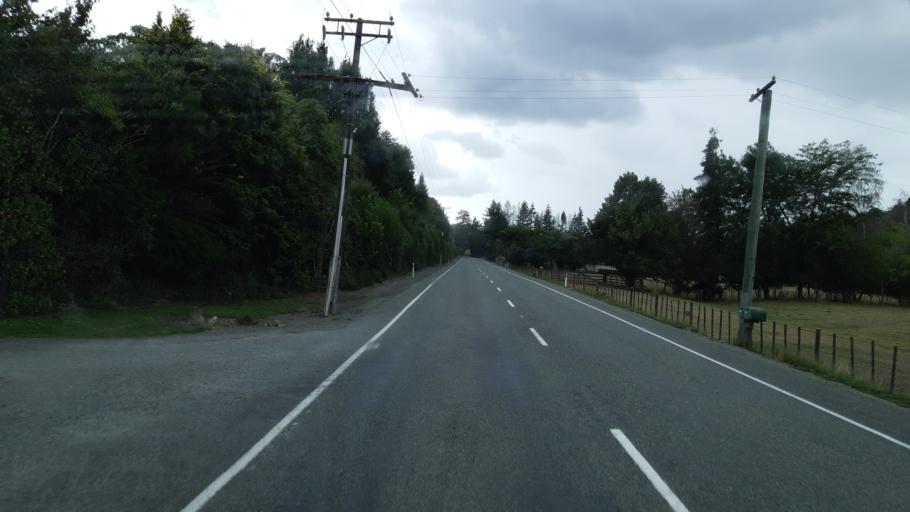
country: NZ
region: Tasman
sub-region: Tasman District
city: Wakefield
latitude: -41.4130
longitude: 173.0166
